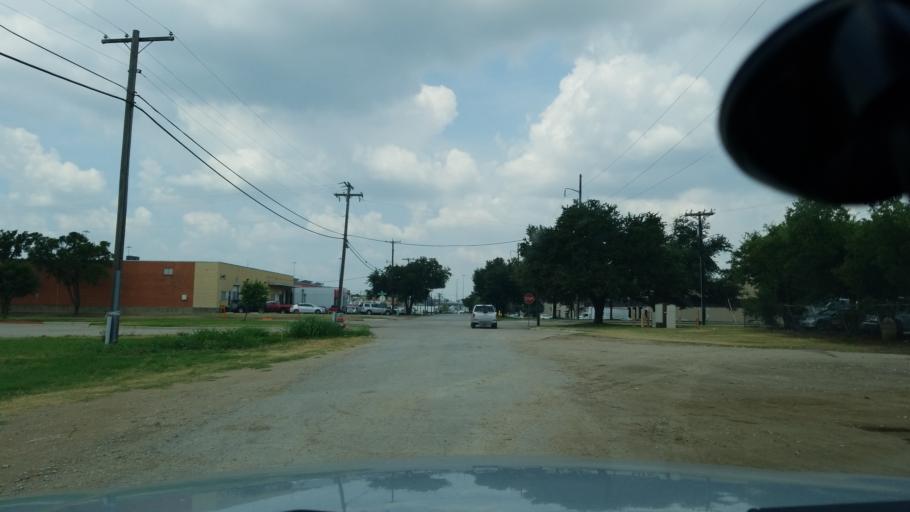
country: US
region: Texas
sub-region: Dallas County
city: Irving
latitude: 32.8369
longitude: -96.8924
